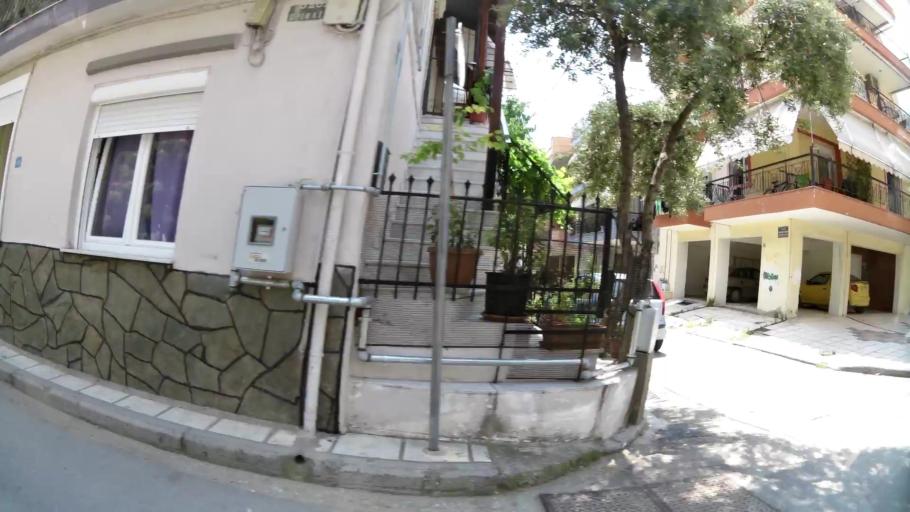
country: GR
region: Central Macedonia
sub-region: Nomos Thessalonikis
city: Evosmos
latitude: 40.6664
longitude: 22.9064
